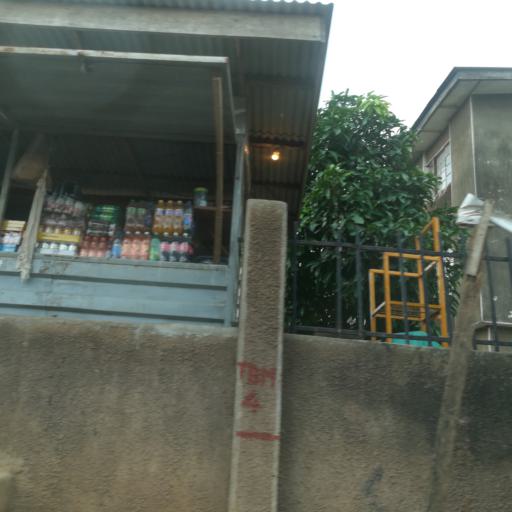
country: NG
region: Lagos
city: Agege
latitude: 6.5919
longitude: 3.2964
